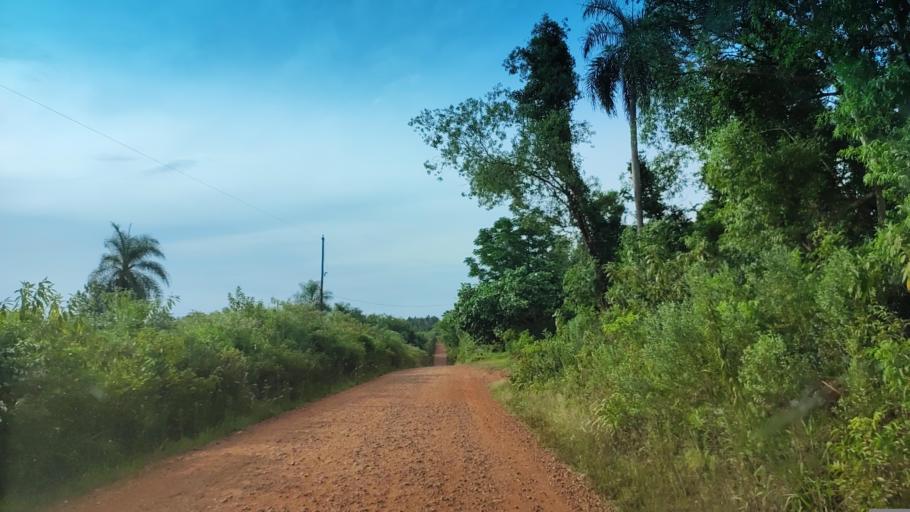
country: AR
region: Misiones
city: Gobernador Roca
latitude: -27.1612
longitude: -55.5194
